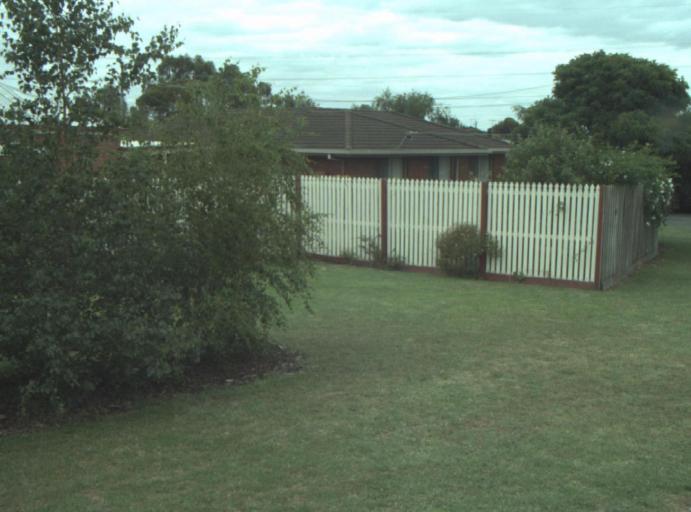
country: AU
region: Victoria
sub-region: Greater Geelong
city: Breakwater
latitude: -38.1993
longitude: 144.3351
